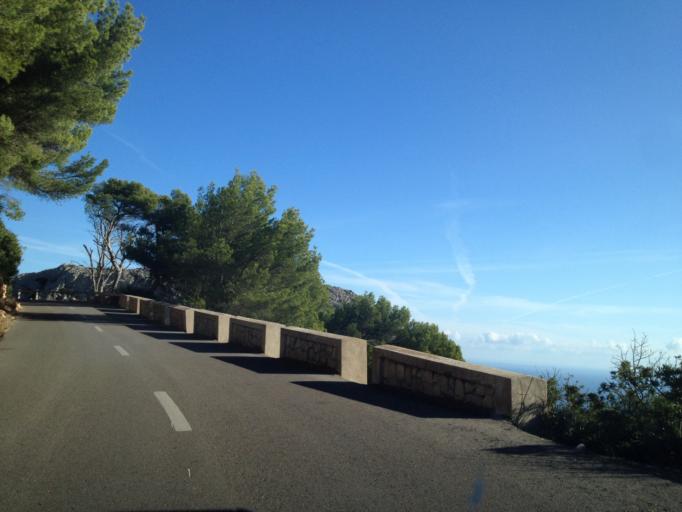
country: ES
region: Balearic Islands
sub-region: Illes Balears
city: Alcudia
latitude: 39.9537
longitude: 3.2071
